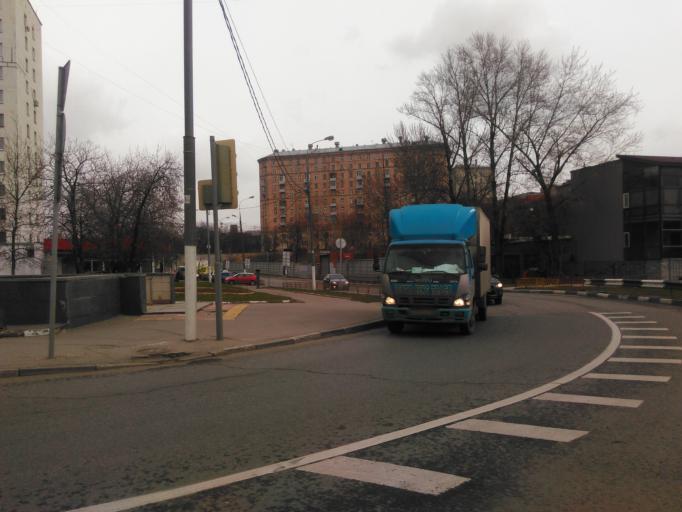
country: RU
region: Moscow
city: Novyye Cheremushki
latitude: 55.7014
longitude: 37.6160
